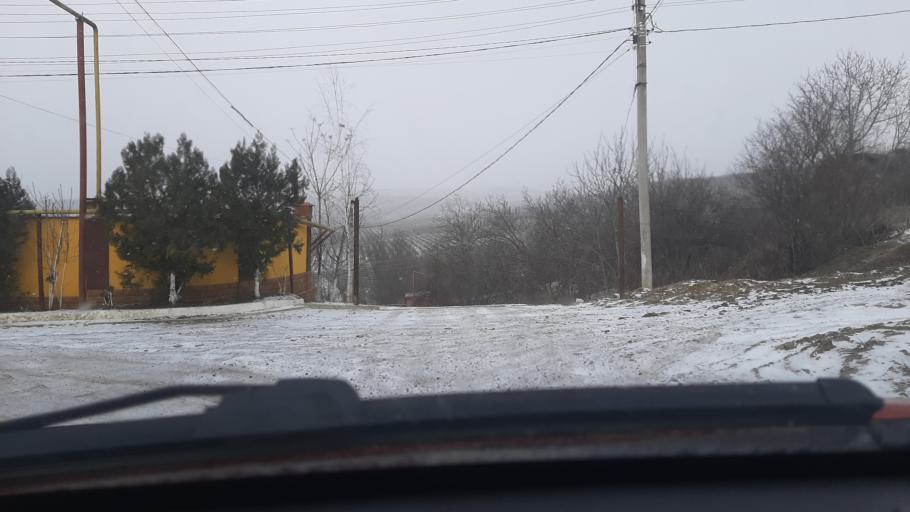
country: MD
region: Laloveni
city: Ialoveni
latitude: 46.9954
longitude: 28.7787
